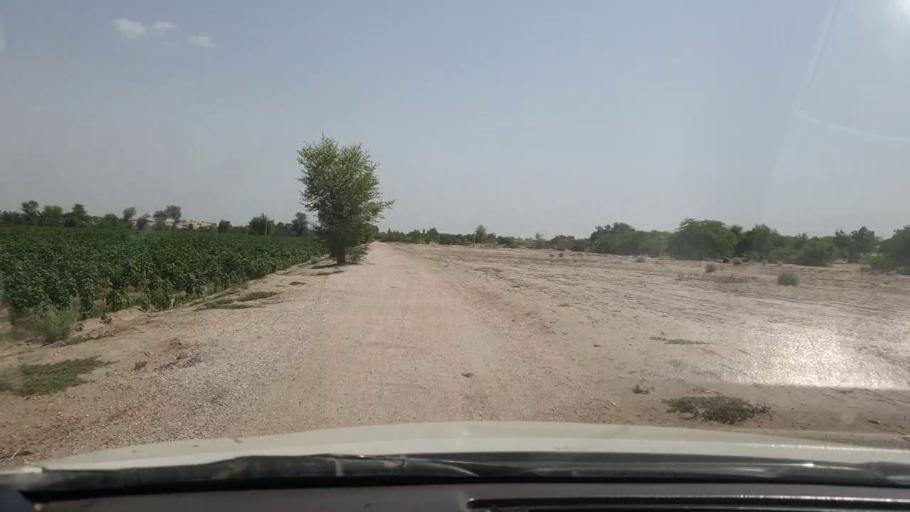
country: PK
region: Sindh
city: Rohri
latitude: 27.4688
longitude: 69.0789
